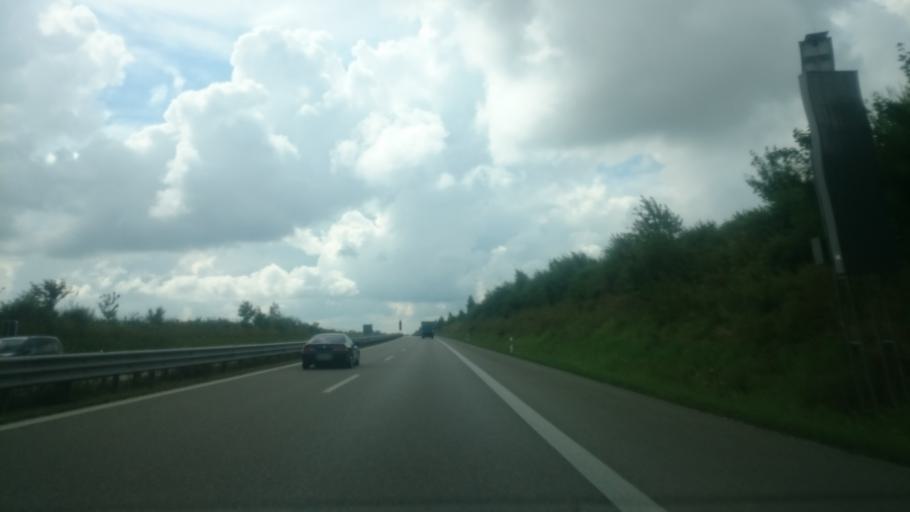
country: DE
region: Bavaria
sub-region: Upper Bavaria
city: Hurlach
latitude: 48.1233
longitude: 10.8330
